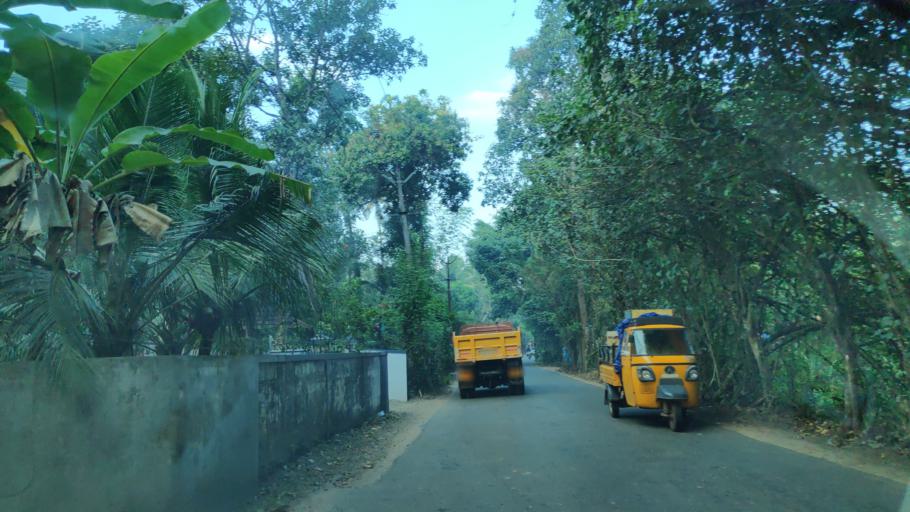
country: IN
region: Kerala
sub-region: Alappuzha
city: Shertallai
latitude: 9.6674
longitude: 76.3882
